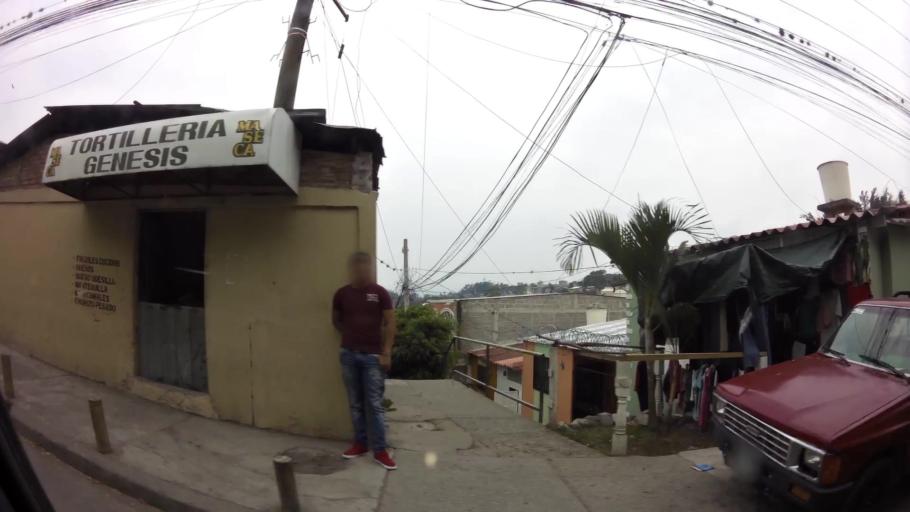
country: HN
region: Francisco Morazan
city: Tegucigalpa
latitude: 14.0769
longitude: -87.2276
